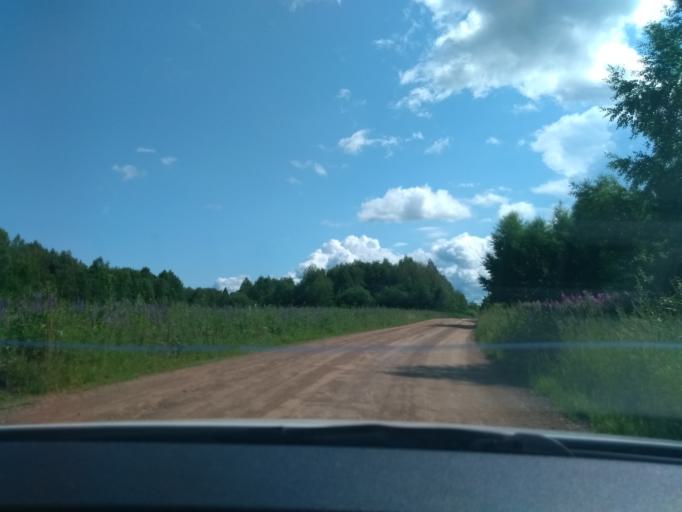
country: RU
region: Perm
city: Sylva
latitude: 57.8265
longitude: 56.7490
